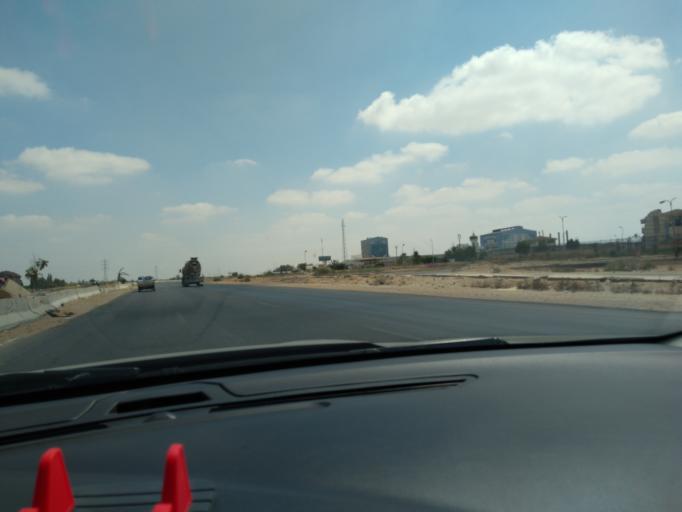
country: EG
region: Al Isma'iliyah
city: At Tall al Kabir
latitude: 30.3409
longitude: 31.8662
